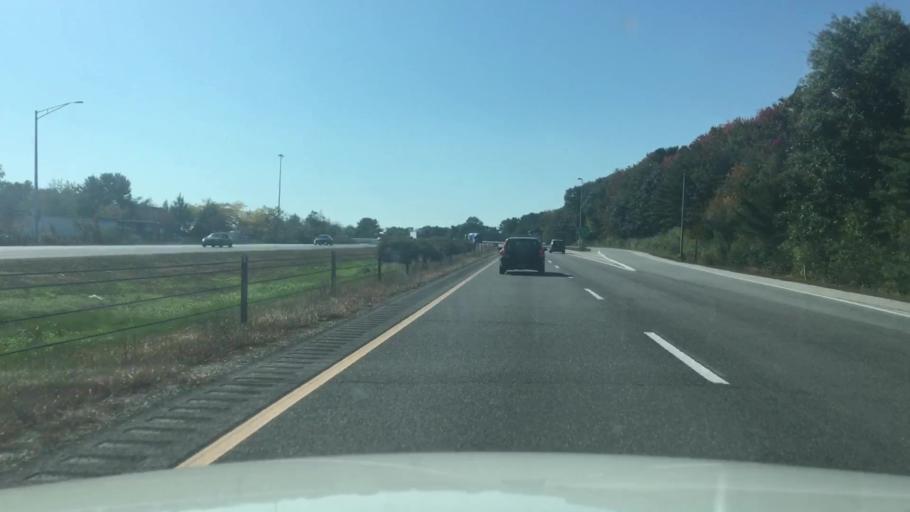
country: US
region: Maine
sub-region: Cumberland County
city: Yarmouth
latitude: 43.8111
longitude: -70.1606
